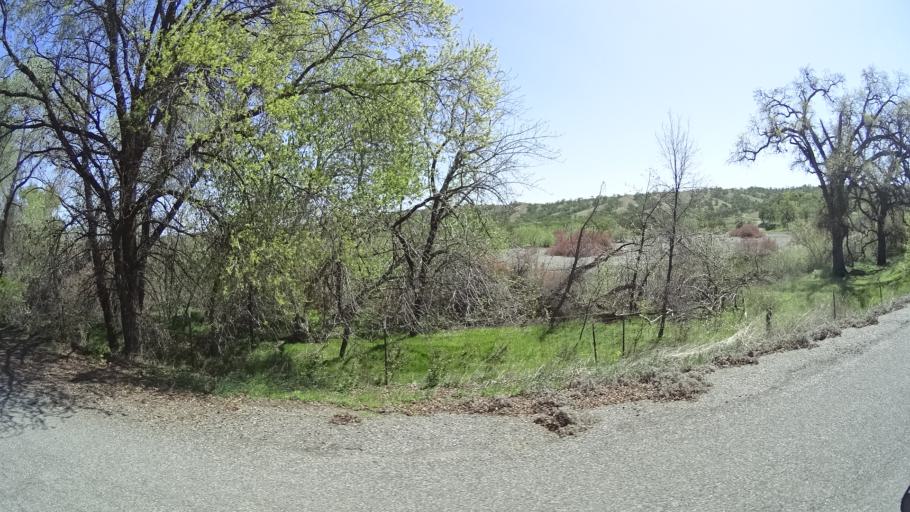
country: US
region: California
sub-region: Glenn County
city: Orland
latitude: 39.7352
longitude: -122.4135
